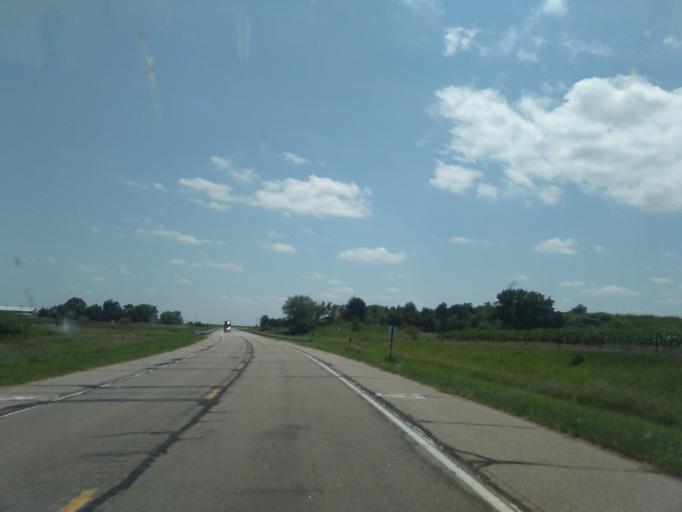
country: US
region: Nebraska
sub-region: Dawson County
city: Lexington
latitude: 40.6950
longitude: -99.7943
